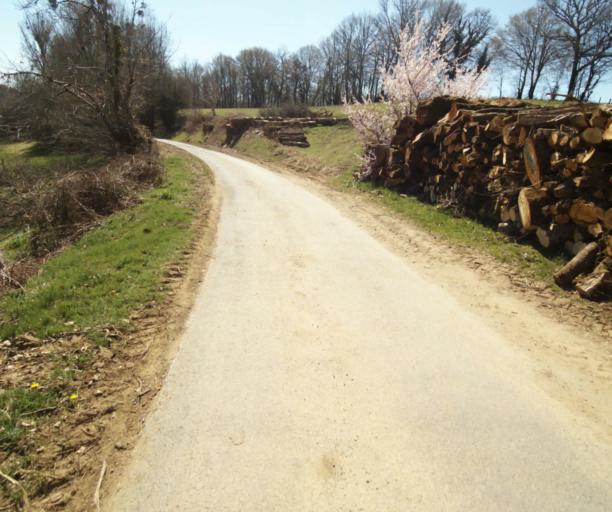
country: FR
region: Limousin
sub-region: Departement de la Correze
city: Saint-Clement
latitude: 45.3202
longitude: 1.7025
